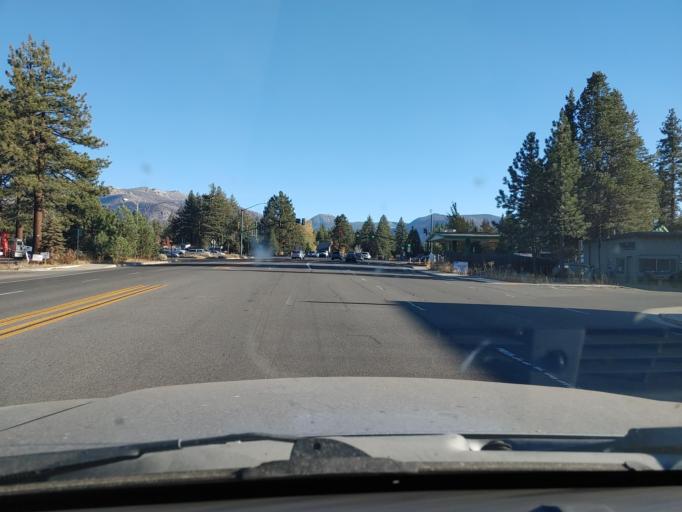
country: US
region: California
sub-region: El Dorado County
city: South Lake Tahoe
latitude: 38.9144
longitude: -120.0055
